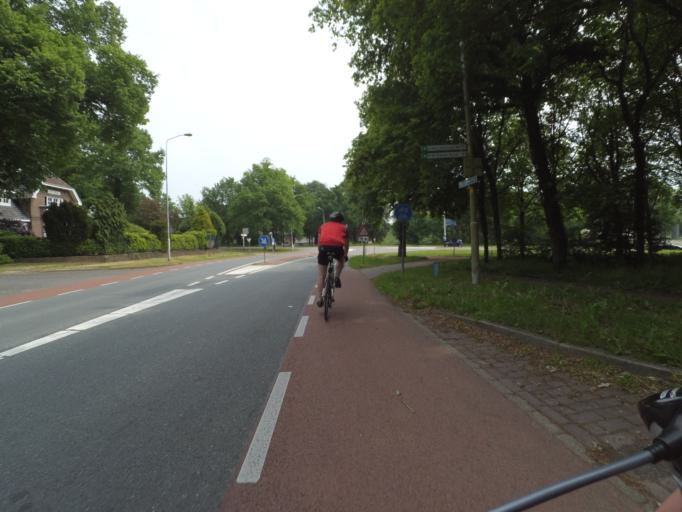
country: NL
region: Gelderland
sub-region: Gemeente Renkum
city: Heelsum
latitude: 51.9825
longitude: 5.7613
